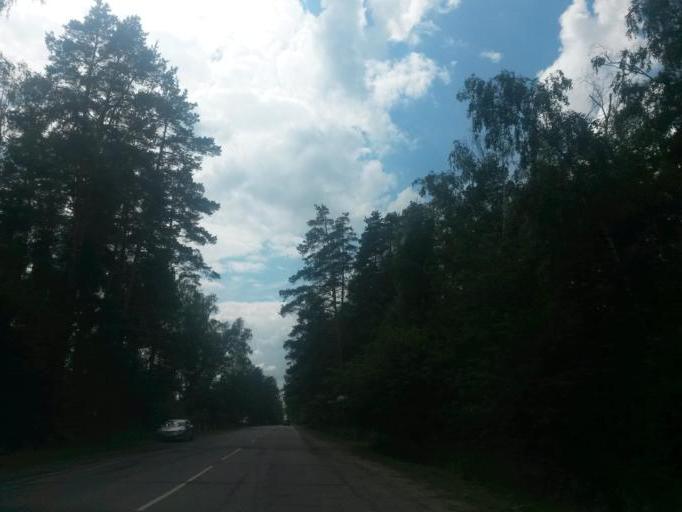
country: RU
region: Moskovskaya
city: Gorki-Leninskiye
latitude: 55.5123
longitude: 37.8258
